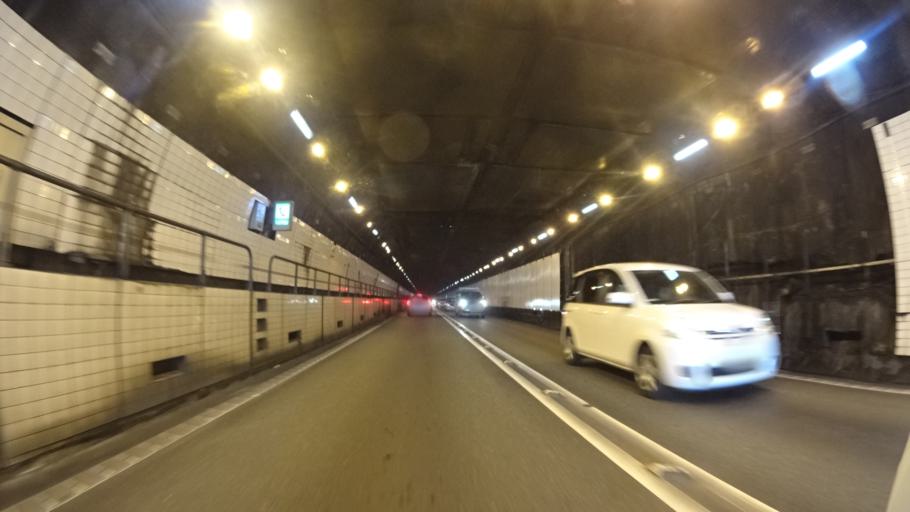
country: JP
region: Yamaguchi
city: Shimonoseki
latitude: 33.9750
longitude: 130.9476
